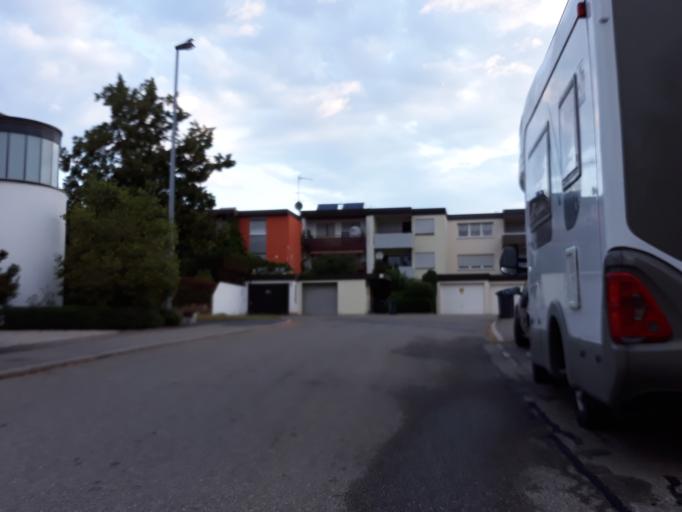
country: DE
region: Baden-Wuerttemberg
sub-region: Regierungsbezirk Stuttgart
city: Schonaich
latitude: 48.6661
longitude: 9.0622
